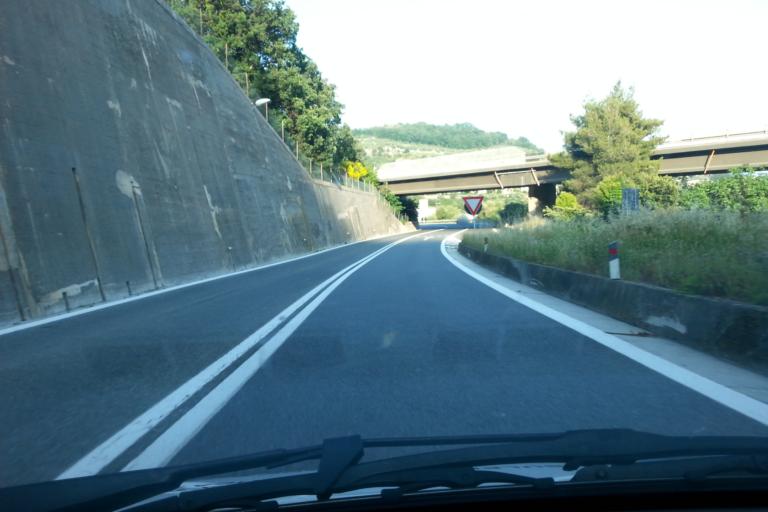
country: IT
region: Liguria
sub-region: Provincia di Savona
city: Pietra Ligure
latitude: 44.1553
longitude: 8.2661
